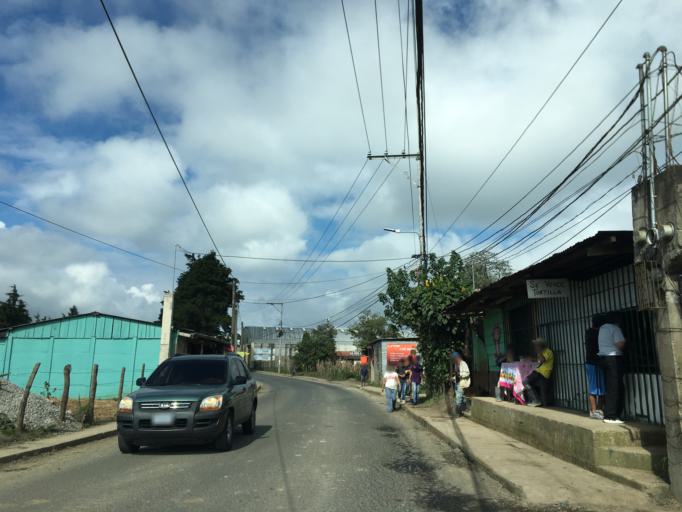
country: GT
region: Guatemala
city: San Jose Pinula
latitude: 14.5562
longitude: -90.4376
